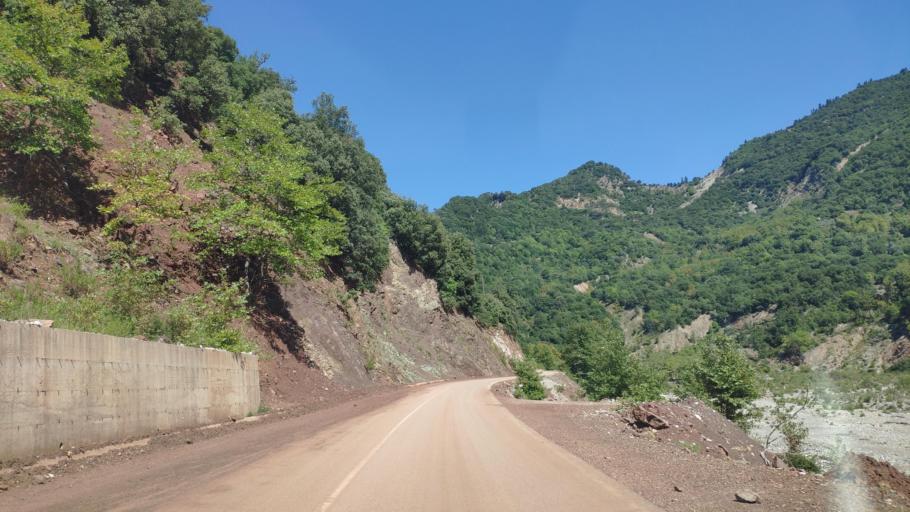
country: GR
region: Central Greece
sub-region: Nomos Evrytanias
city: Kerasochori
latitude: 39.0658
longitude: 21.6066
